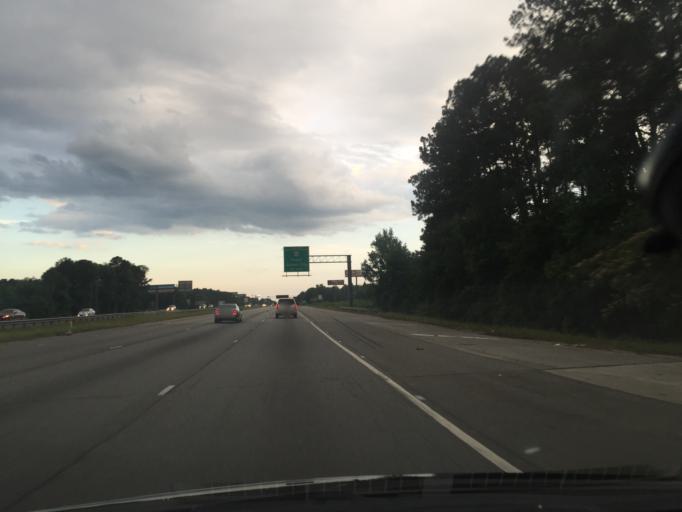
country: US
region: Georgia
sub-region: Chatham County
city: Pooler
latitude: 32.1316
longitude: -81.2400
